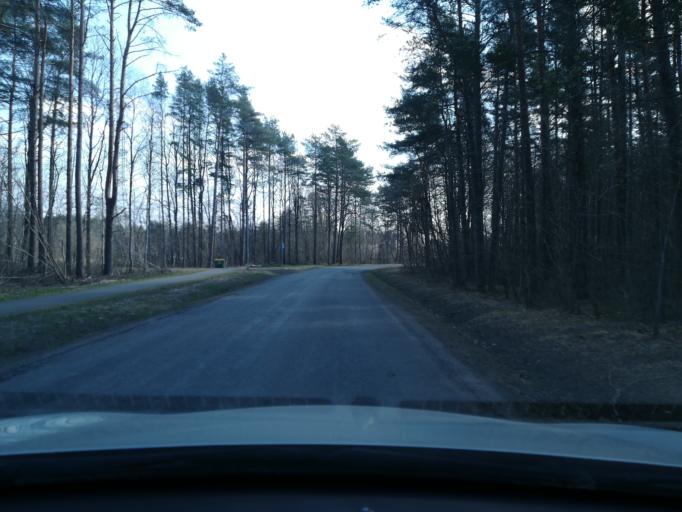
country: EE
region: Harju
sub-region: Saue vald
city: Laagri
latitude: 59.3545
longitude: 24.5854
